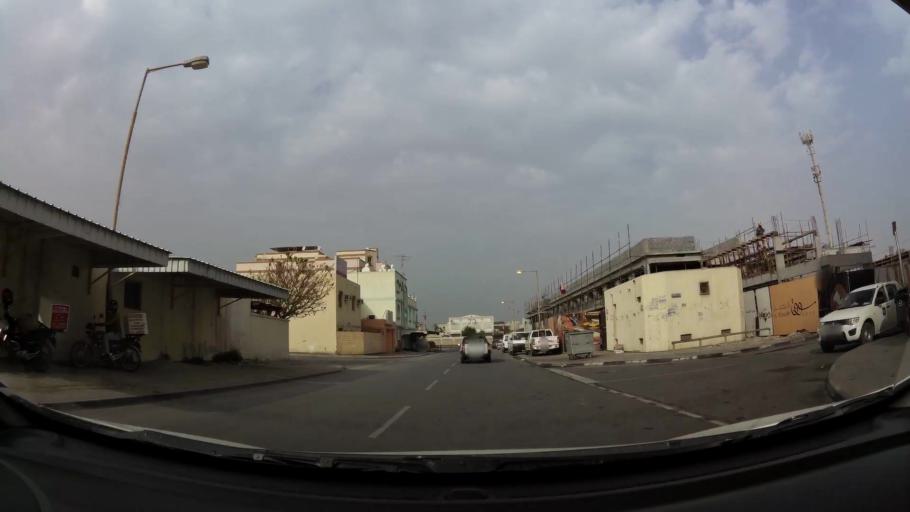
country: BH
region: Northern
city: Ar Rifa'
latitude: 26.1383
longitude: 50.5703
